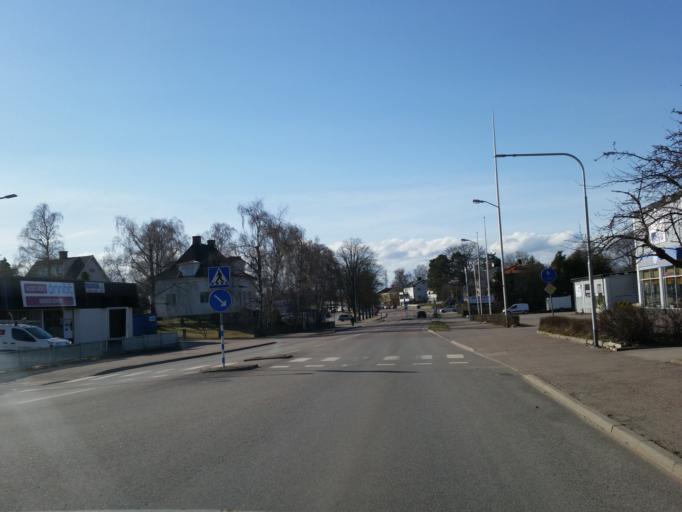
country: SE
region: Kalmar
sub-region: Oskarshamns Kommun
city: Oskarshamn
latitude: 57.2644
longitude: 16.4393
